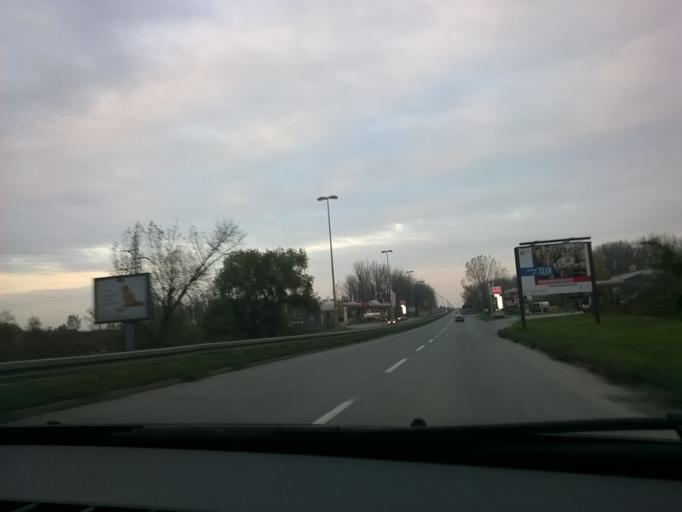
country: RS
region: Autonomna Pokrajina Vojvodina
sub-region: Juznobacki Okrug
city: Novi Sad
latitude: 45.2766
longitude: 19.8501
